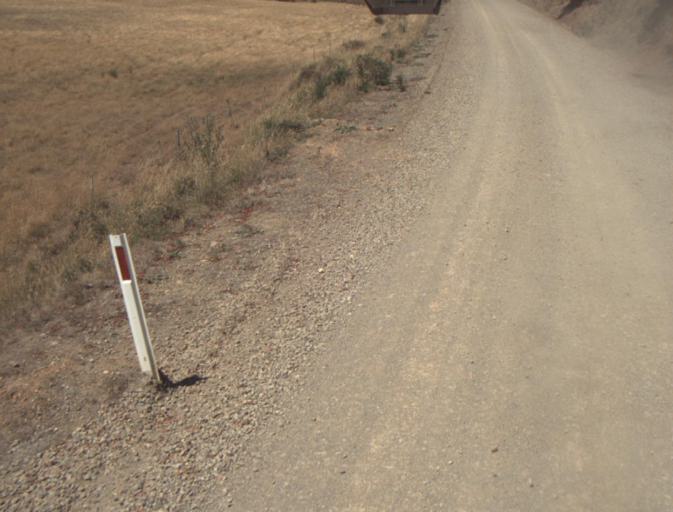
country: AU
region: Tasmania
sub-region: Dorset
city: Scottsdale
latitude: -41.3055
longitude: 147.3679
